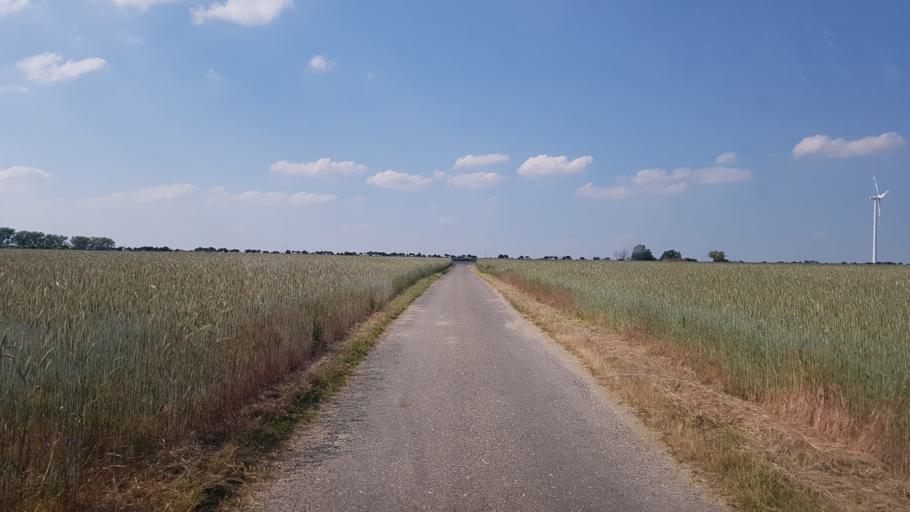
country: DE
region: Brandenburg
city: Trobitz
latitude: 51.6611
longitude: 13.4395
